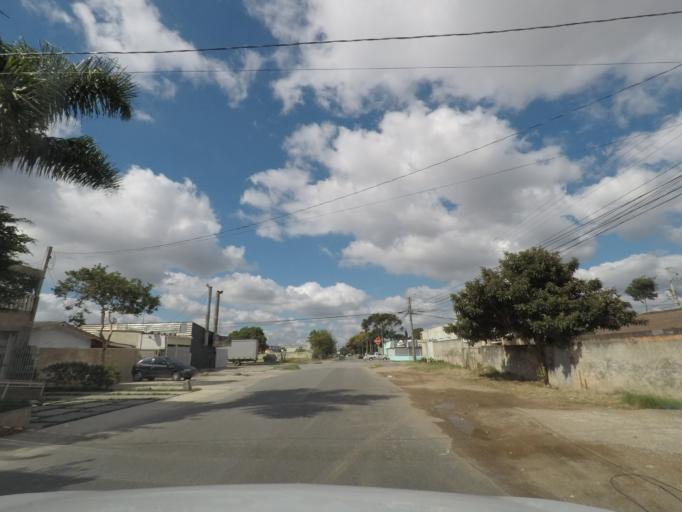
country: BR
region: Parana
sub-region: Sao Jose Dos Pinhais
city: Sao Jose dos Pinhais
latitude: -25.5094
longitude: -49.2209
